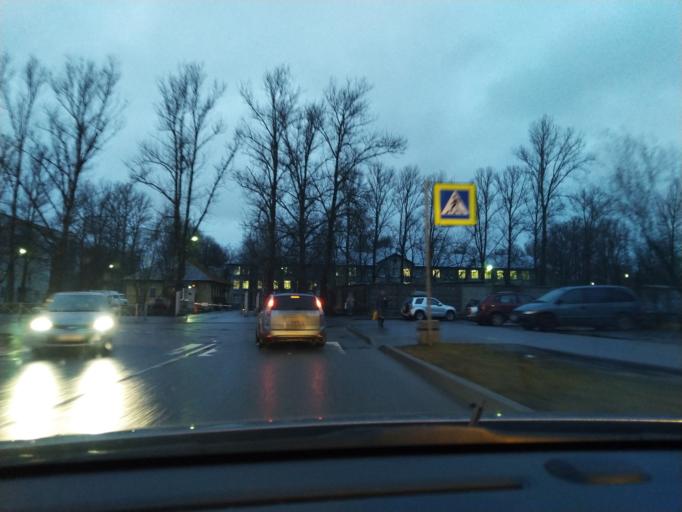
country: RU
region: St.-Petersburg
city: Uritsk
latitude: 59.8388
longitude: 30.1833
